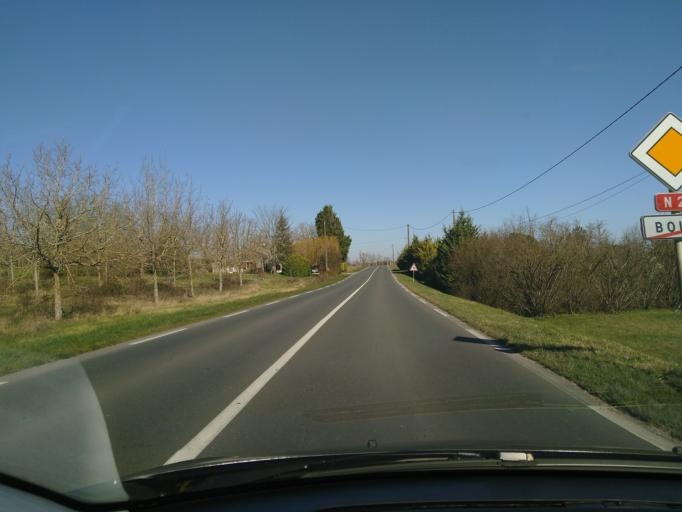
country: FR
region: Aquitaine
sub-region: Departement de la Dordogne
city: Monbazillac
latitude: 44.7640
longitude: 0.5264
